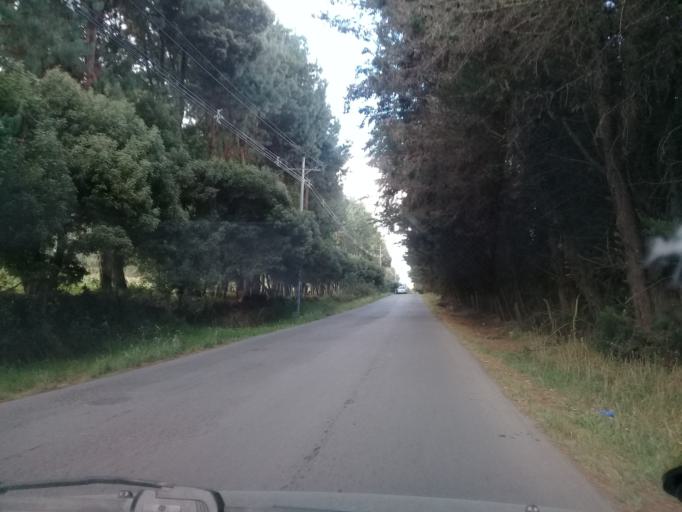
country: CO
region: Cundinamarca
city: Subachoque
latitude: 4.9080
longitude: -74.1881
